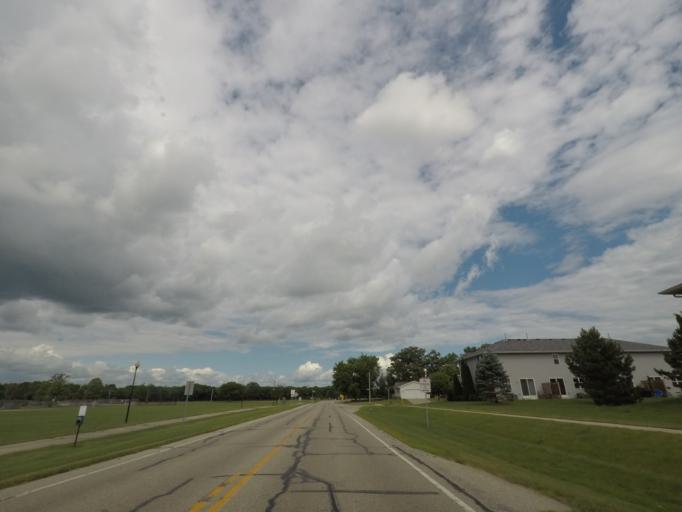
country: US
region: Wisconsin
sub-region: Dane County
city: Belleville
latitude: 42.8567
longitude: -89.5271
